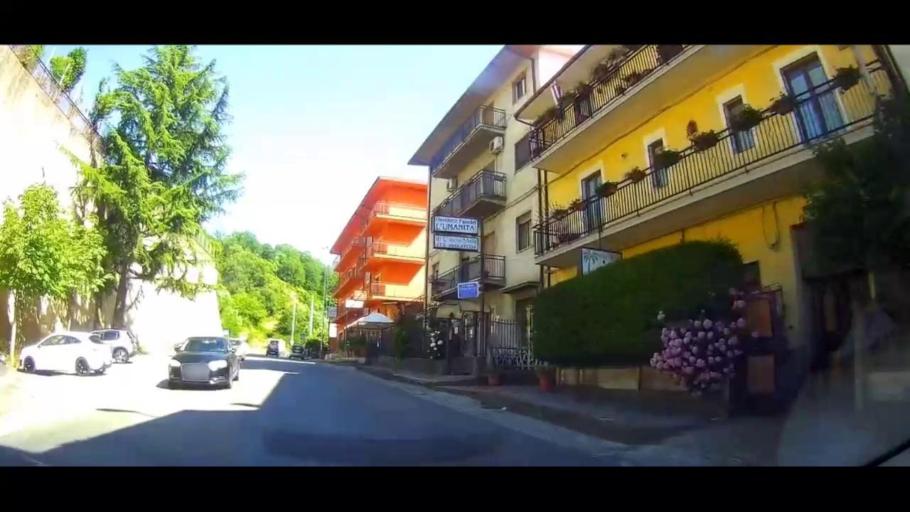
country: IT
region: Calabria
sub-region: Provincia di Cosenza
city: Spezzano della Sila
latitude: 39.3030
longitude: 16.3401
